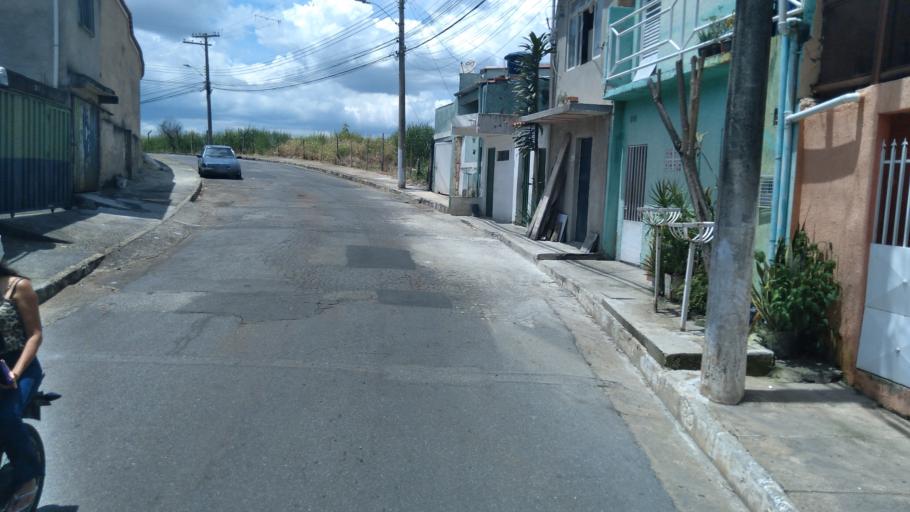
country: BR
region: Minas Gerais
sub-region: Contagem
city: Contagem
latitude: -19.9176
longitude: -44.0074
